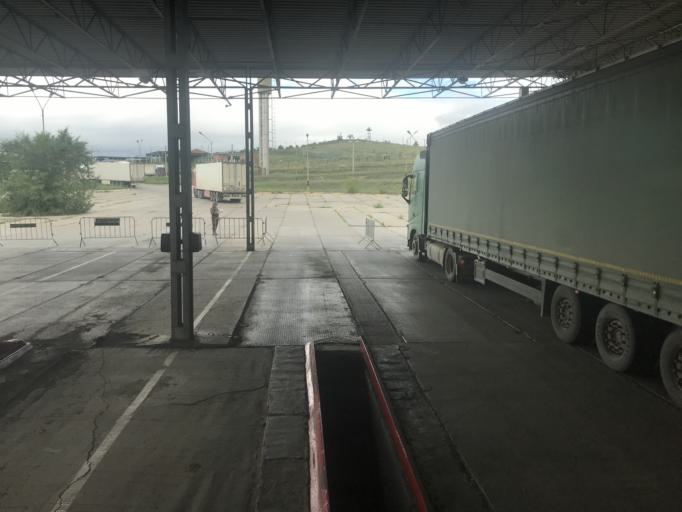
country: MN
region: Selenge
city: Altanbulag
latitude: 50.3220
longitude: 106.4903
